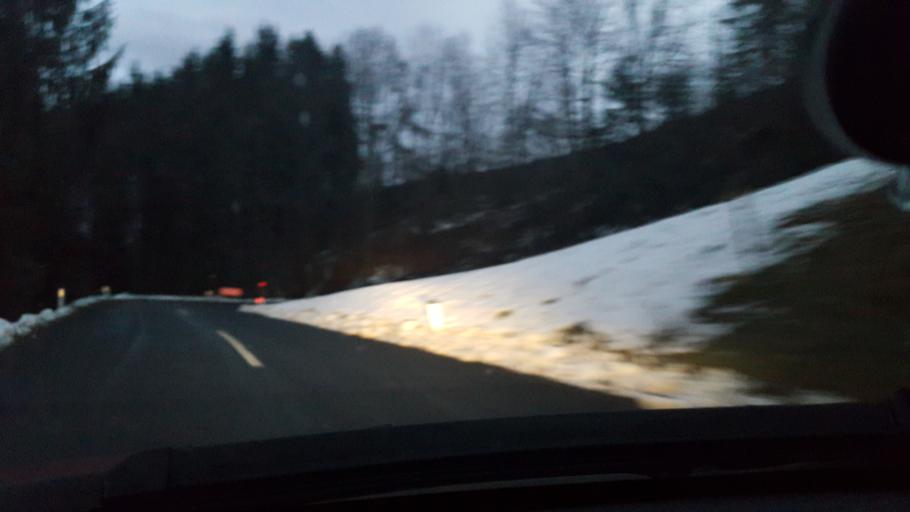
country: AT
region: Styria
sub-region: Politischer Bezirk Leibnitz
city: Sulztal an der Weinstrasse
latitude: 46.6442
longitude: 15.5178
